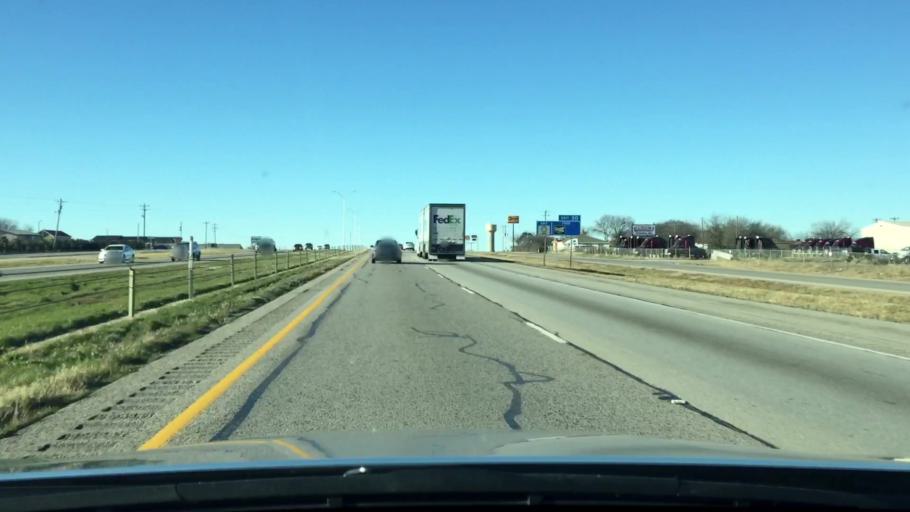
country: US
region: Texas
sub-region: Johnson County
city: Alvarado
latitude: 32.4580
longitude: -97.2618
